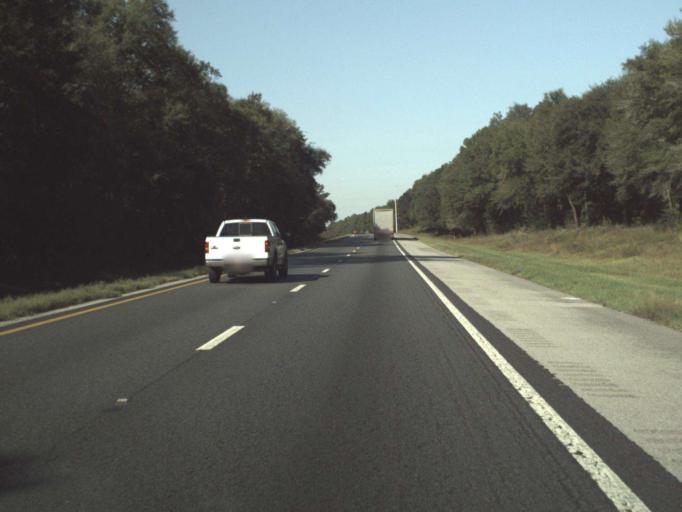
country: US
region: Florida
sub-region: Holmes County
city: Bonifay
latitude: 30.7614
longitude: -85.7864
